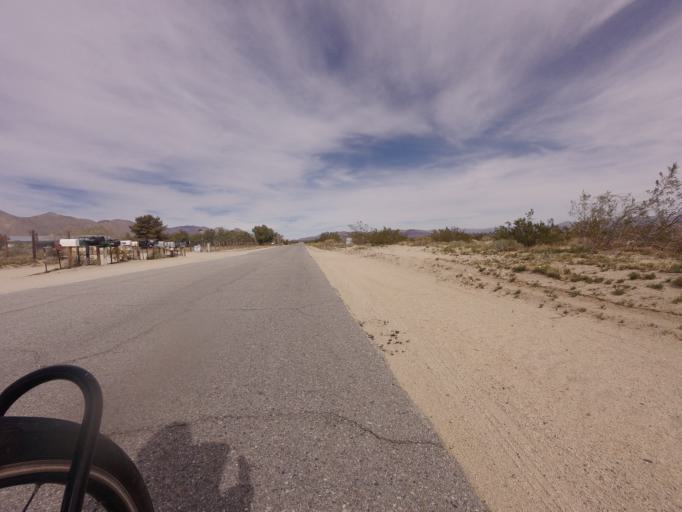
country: US
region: California
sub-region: Kern County
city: Inyokern
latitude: 35.7614
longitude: -117.8463
